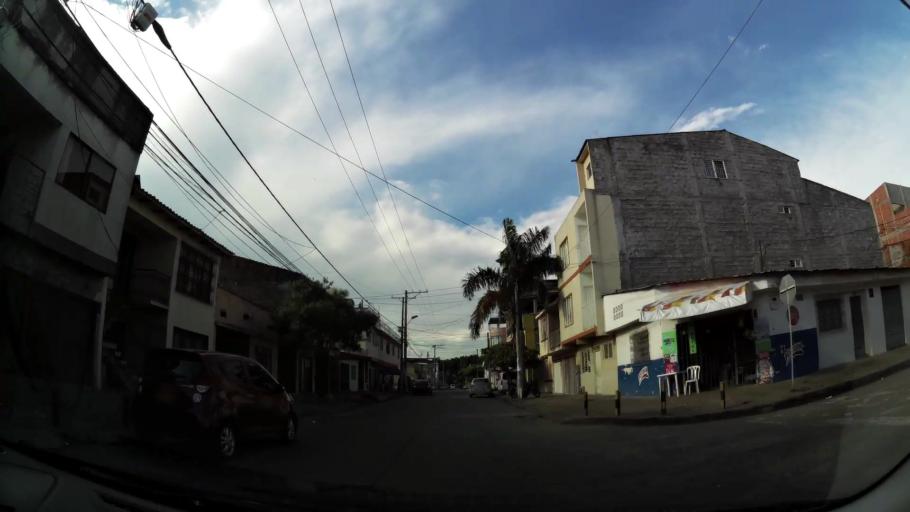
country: CO
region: Valle del Cauca
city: Cali
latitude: 3.4263
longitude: -76.5244
